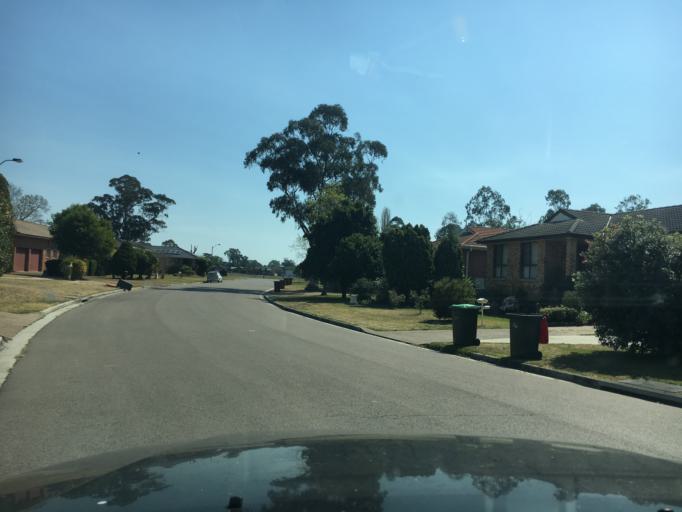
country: AU
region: New South Wales
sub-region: Singleton
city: Singleton
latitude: -32.5686
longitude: 151.1885
